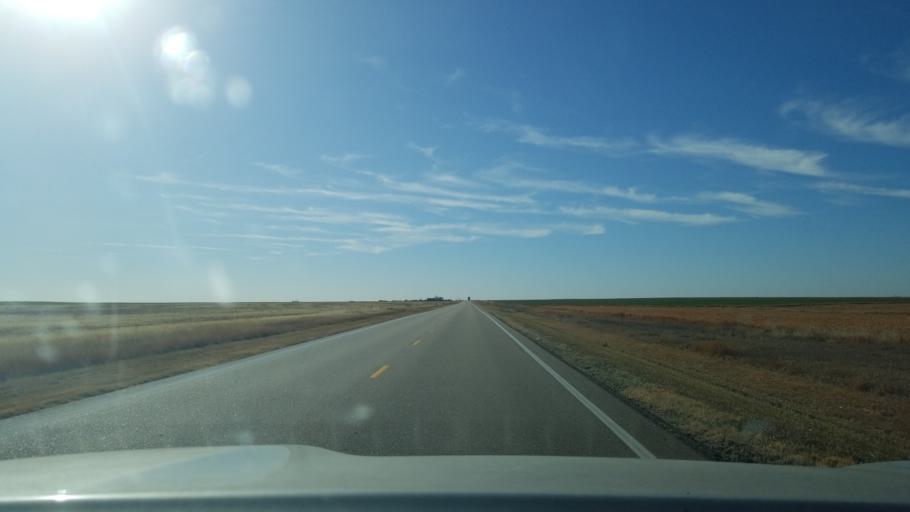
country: US
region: Kansas
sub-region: Ness County
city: Ness City
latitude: 38.3447
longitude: -99.8978
